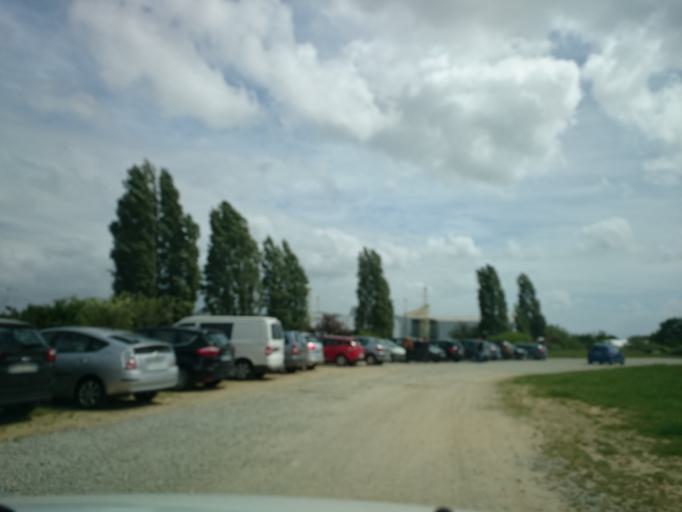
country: FR
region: Brittany
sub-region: Departement du Morbihan
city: Vannes
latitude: 47.6378
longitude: -2.7674
